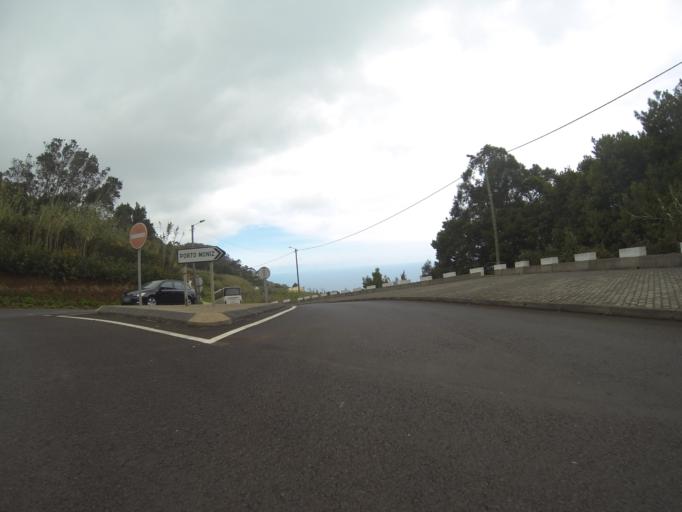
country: PT
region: Madeira
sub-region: Porto Moniz
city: Porto Moniz
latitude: 32.8612
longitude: -17.1746
